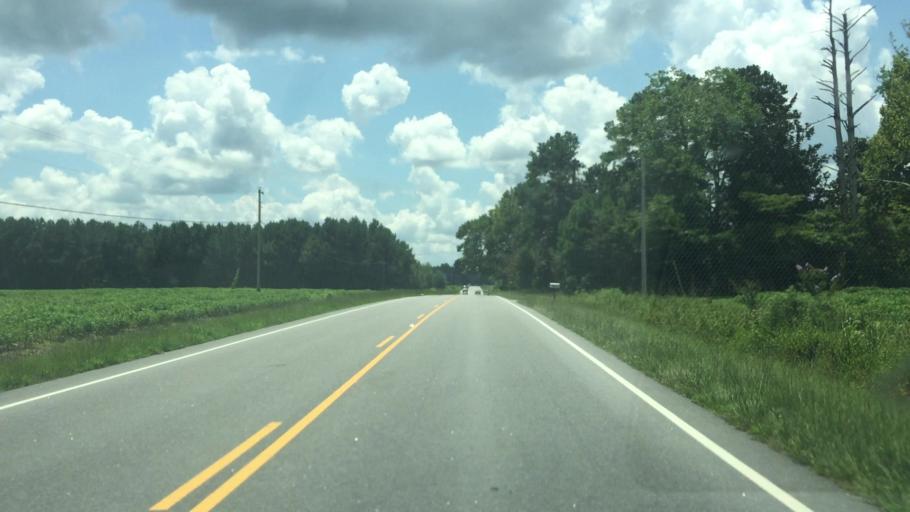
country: US
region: North Carolina
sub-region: Columbus County
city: Chadbourn
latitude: 34.2676
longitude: -78.8142
